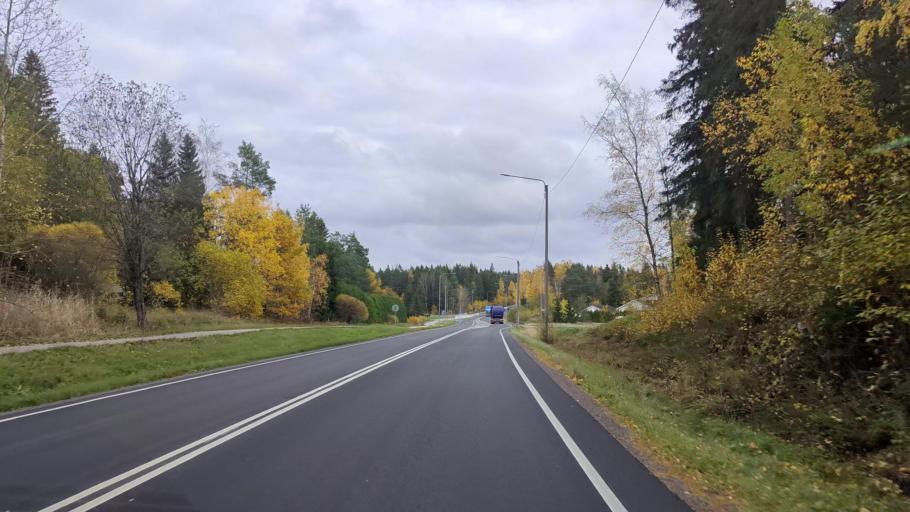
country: FI
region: Varsinais-Suomi
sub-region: Turku
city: Kaarina
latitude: 60.4620
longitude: 22.3562
